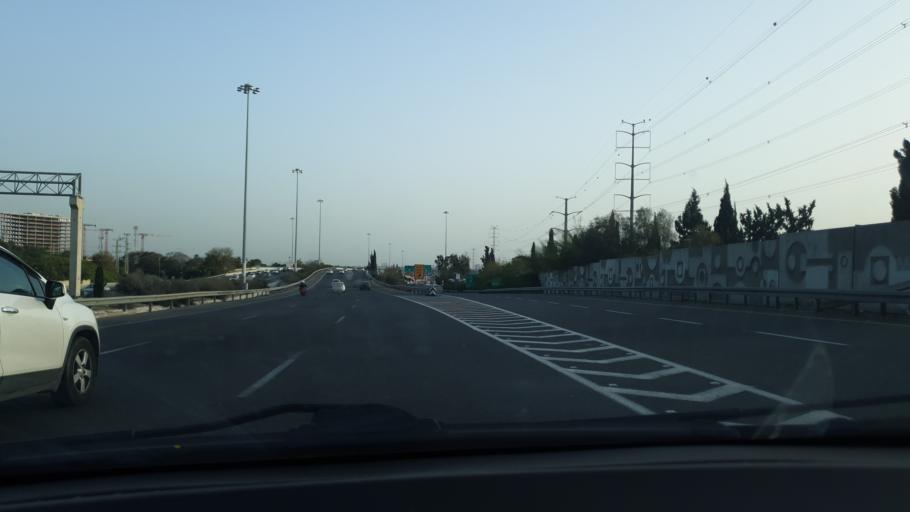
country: IL
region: Tel Aviv
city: Azor
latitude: 32.0418
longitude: 34.8294
